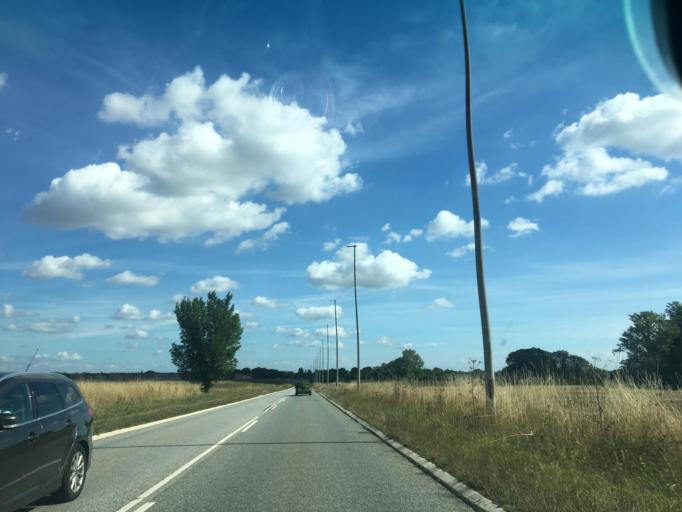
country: DK
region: Zealand
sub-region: Greve Kommune
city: Greve
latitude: 55.5736
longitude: 12.2520
